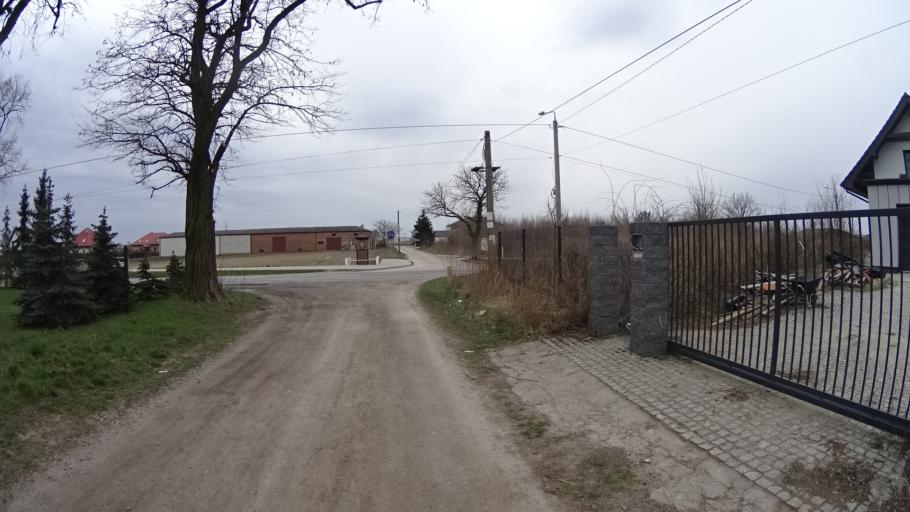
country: PL
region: Masovian Voivodeship
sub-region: Powiat warszawski zachodni
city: Ozarow Mazowiecki
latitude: 52.2307
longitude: 20.7907
